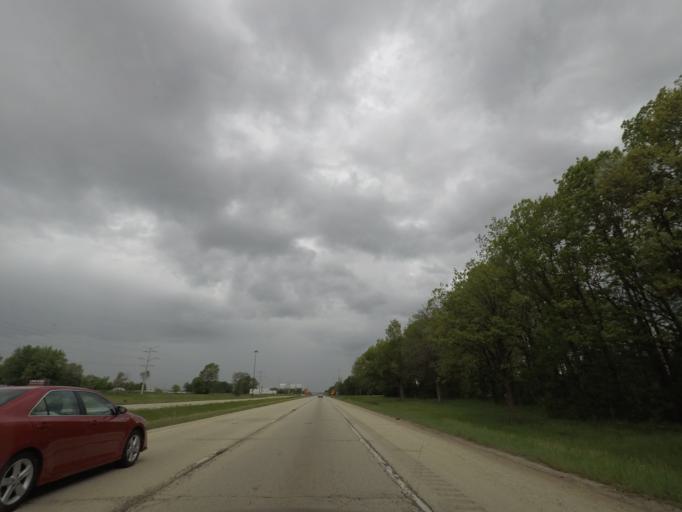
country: US
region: Illinois
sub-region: Winnebago County
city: Cherry Valley
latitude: 42.2203
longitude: -89.0148
